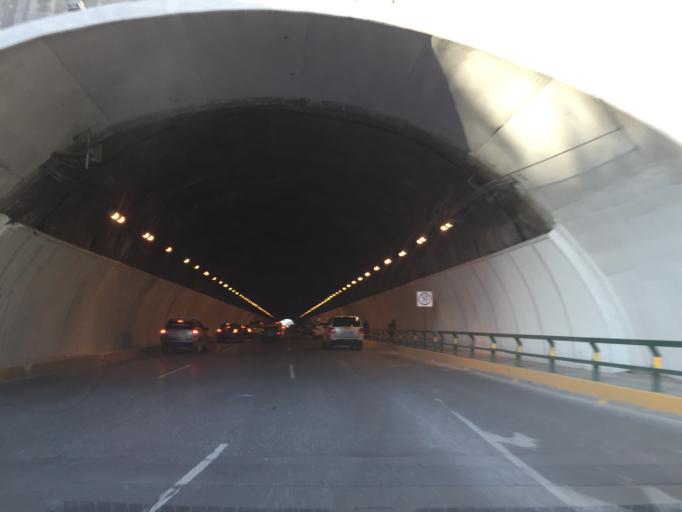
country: MX
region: Nuevo Leon
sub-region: Monterrey
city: Monterrey
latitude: 25.6557
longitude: -100.3374
